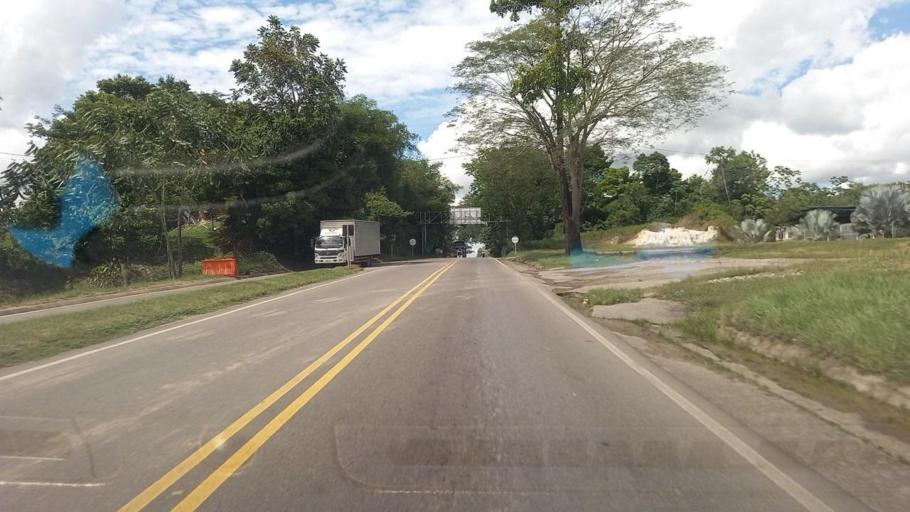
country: CO
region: Santander
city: Barrancabermeja
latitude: 7.1244
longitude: -73.5841
